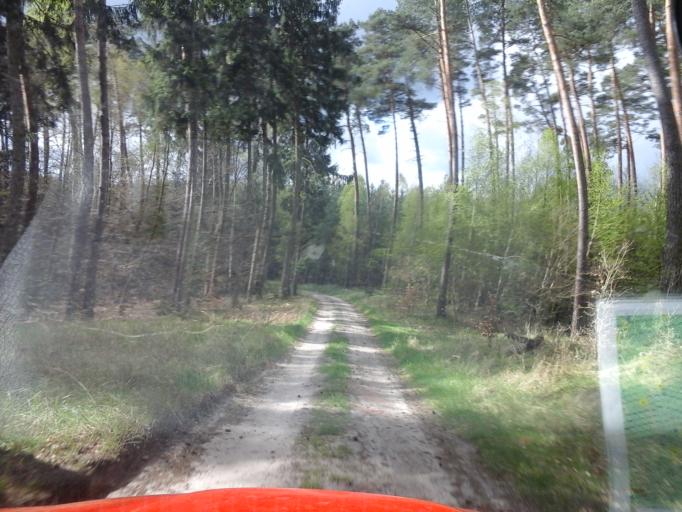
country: PL
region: West Pomeranian Voivodeship
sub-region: Powiat choszczenski
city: Bierzwnik
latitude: 53.0282
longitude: 15.6008
